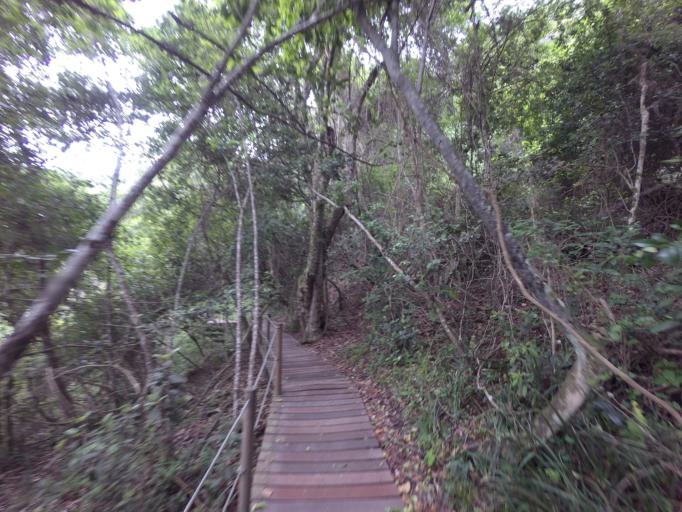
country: ZA
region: Eastern Cape
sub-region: Cacadu District Municipality
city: Kareedouw
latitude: -34.0216
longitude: 23.8975
